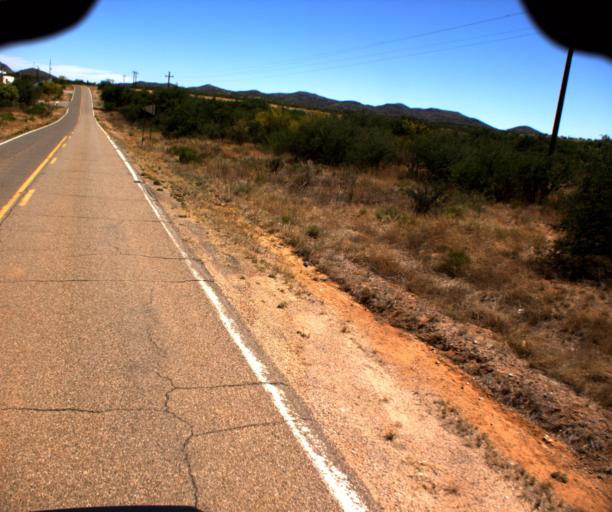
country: US
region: Arizona
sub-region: Santa Cruz County
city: Tubac
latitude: 31.4968
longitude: -111.5461
